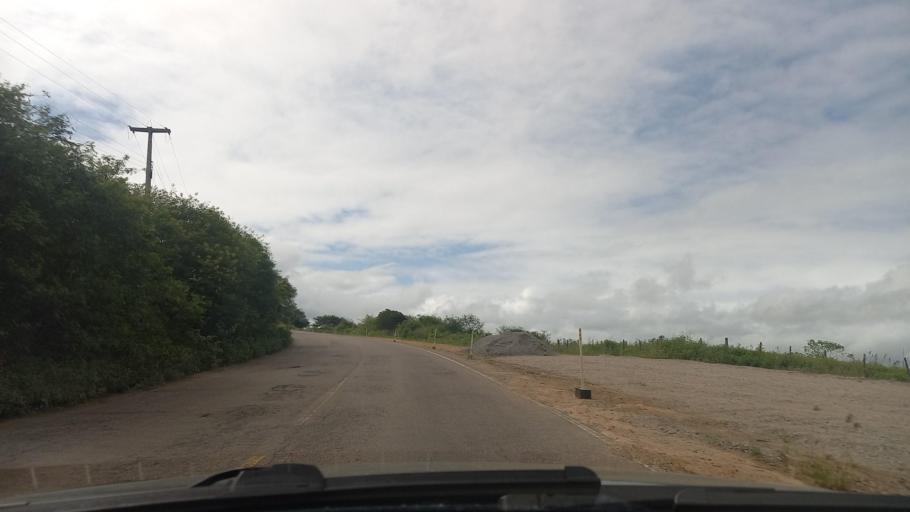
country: BR
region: Alagoas
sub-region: Batalha
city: Batalha
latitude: -9.6633
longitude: -37.1689
